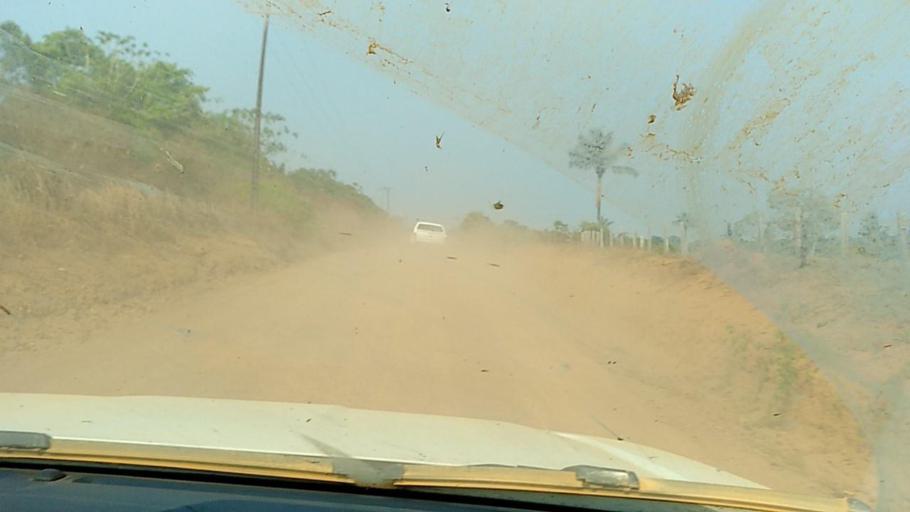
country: BR
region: Rondonia
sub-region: Porto Velho
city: Porto Velho
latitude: -8.8377
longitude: -64.1496
